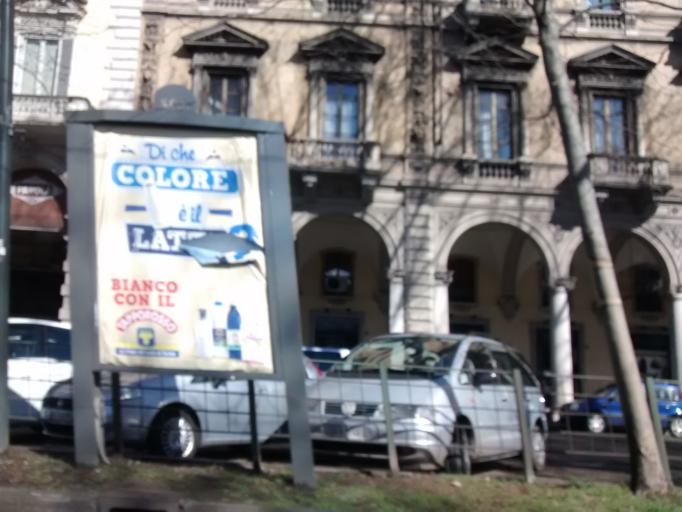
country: IT
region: Piedmont
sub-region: Provincia di Torino
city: Turin
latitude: 45.0648
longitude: 7.6733
